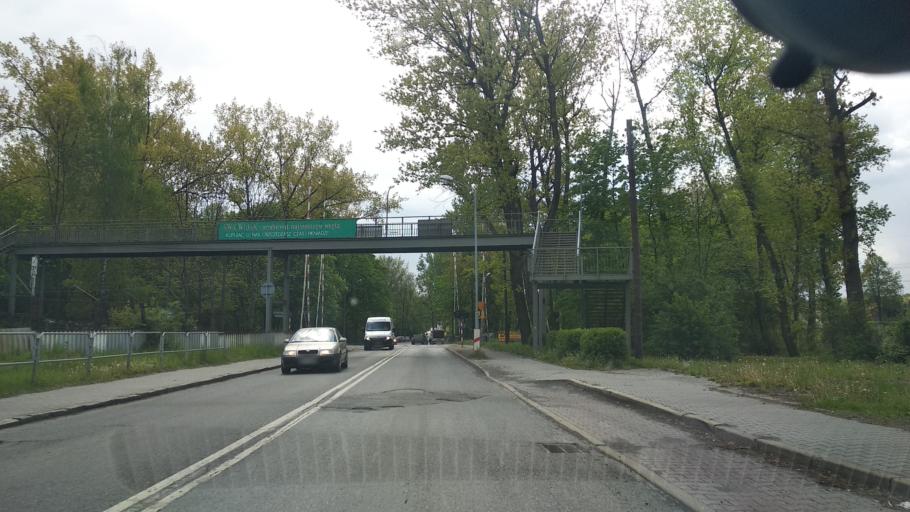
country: PL
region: Silesian Voivodeship
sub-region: Katowice
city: Katowice
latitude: 50.2433
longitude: 18.9827
